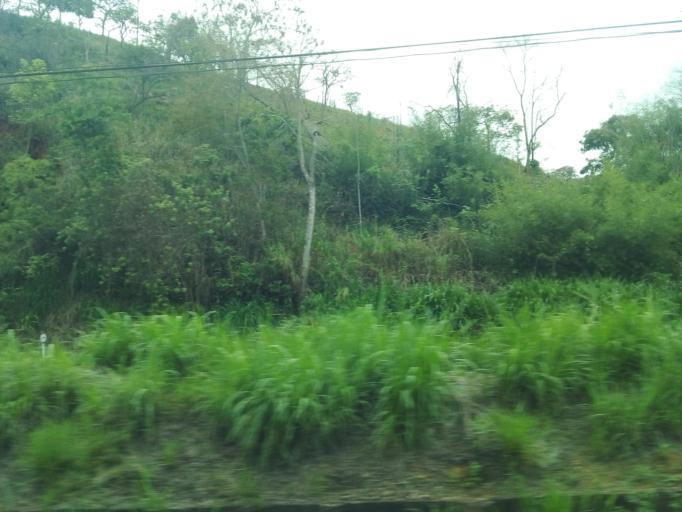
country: BR
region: Minas Gerais
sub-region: Nova Era
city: Nova Era
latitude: -19.7302
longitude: -42.9975
